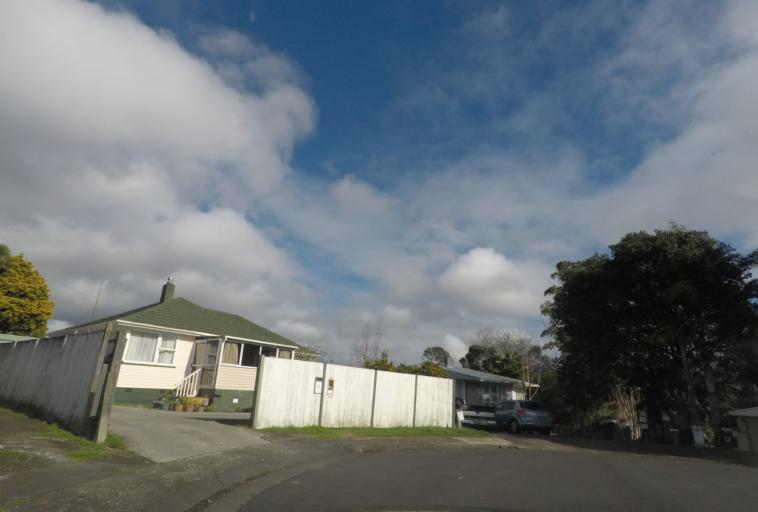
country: NZ
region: Auckland
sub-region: Auckland
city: Rosebank
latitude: -36.8938
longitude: 174.6624
